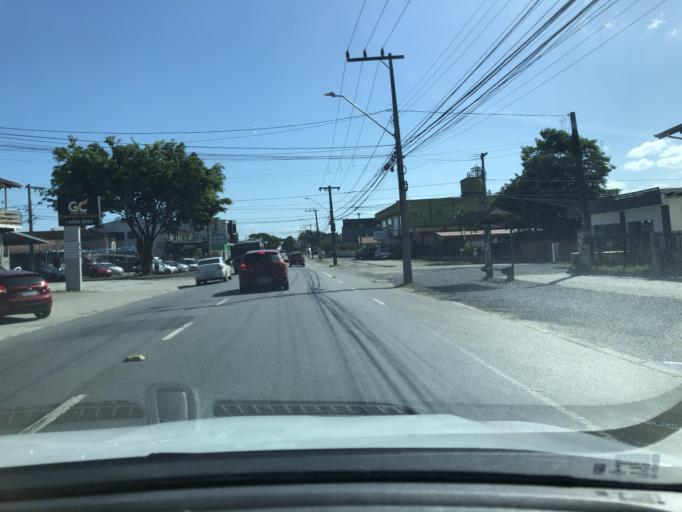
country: BR
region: Santa Catarina
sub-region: Joinville
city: Joinville
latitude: -26.3192
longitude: -48.8307
